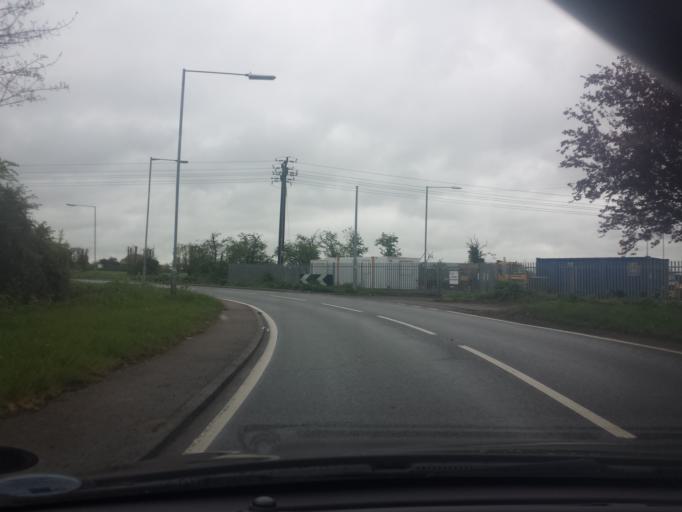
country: GB
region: England
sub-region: Suffolk
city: East Bergholt
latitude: 51.9262
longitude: 0.9921
